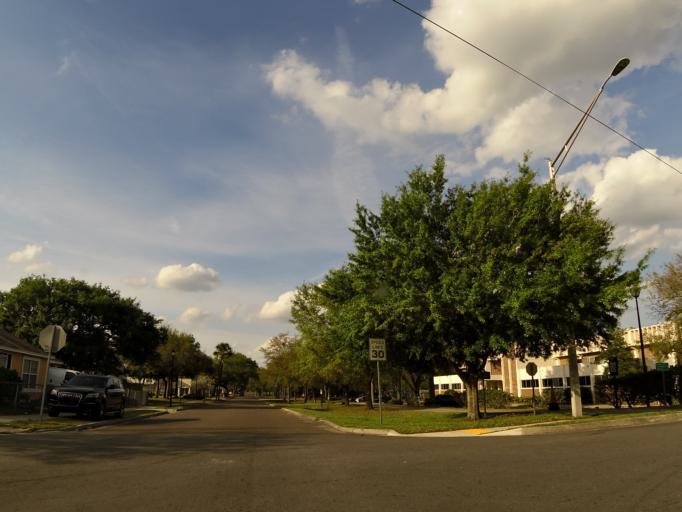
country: US
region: Florida
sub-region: Duval County
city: Jacksonville
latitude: 30.3441
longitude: -81.6715
